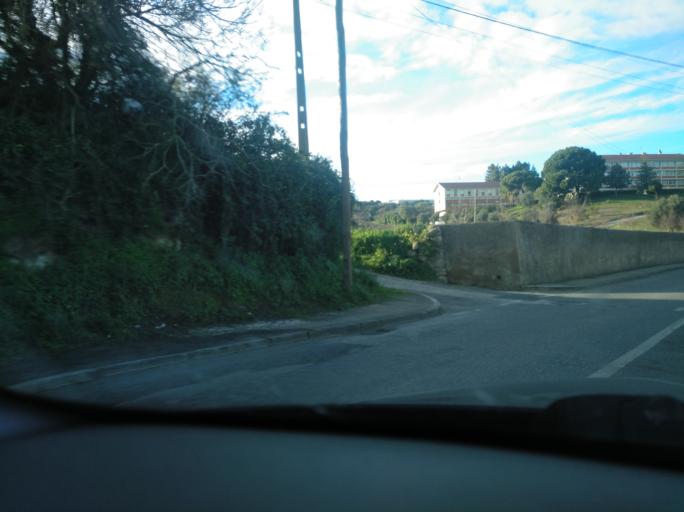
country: PT
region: Lisbon
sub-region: Loures
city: Apelacao
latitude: 38.8107
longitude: -9.1314
